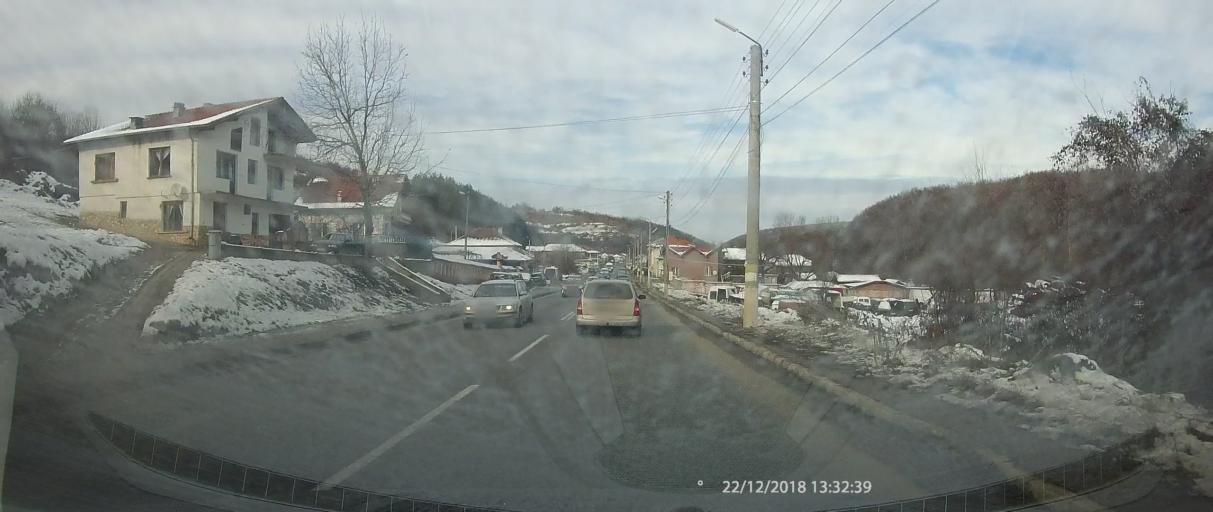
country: BG
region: Lovech
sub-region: Obshtina Yablanitsa
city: Yablanitsa
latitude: 43.1027
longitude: 24.1504
